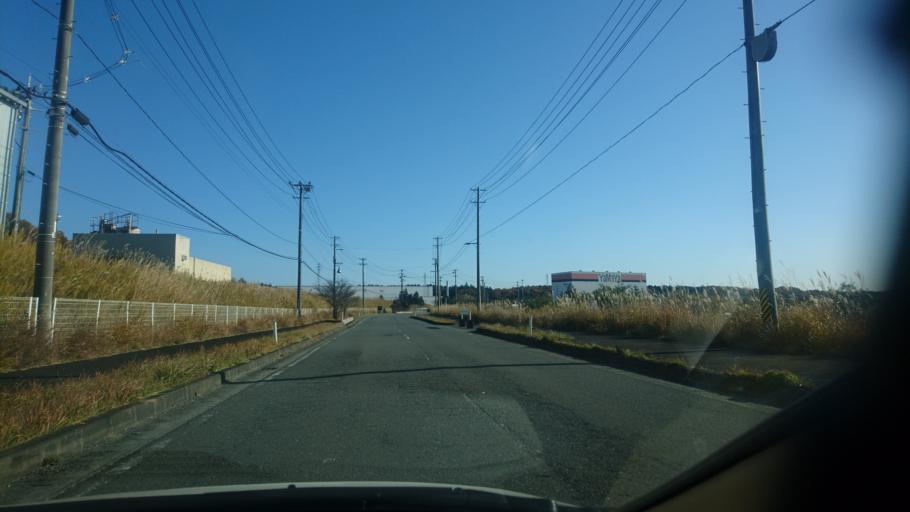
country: JP
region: Miyagi
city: Tomiya
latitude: 38.4607
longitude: 140.9349
